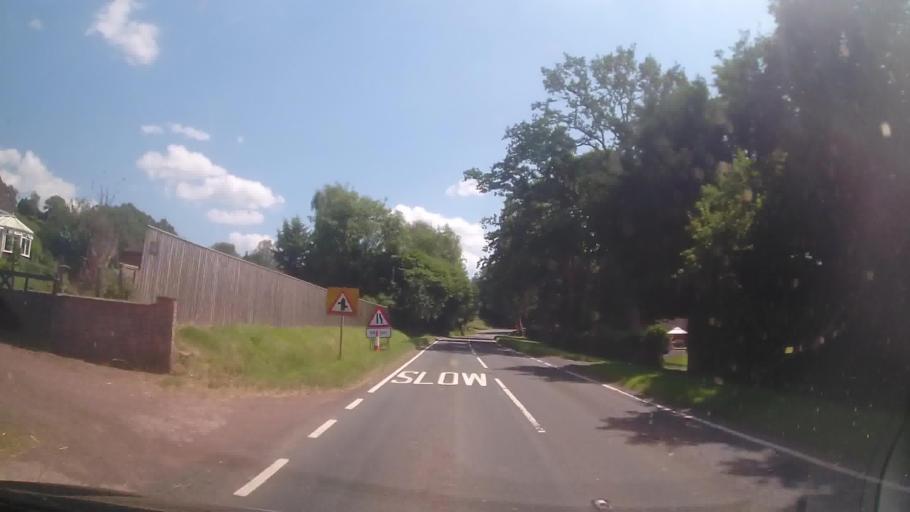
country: GB
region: England
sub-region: Herefordshire
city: Brockhampton
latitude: 51.9773
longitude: -2.5579
